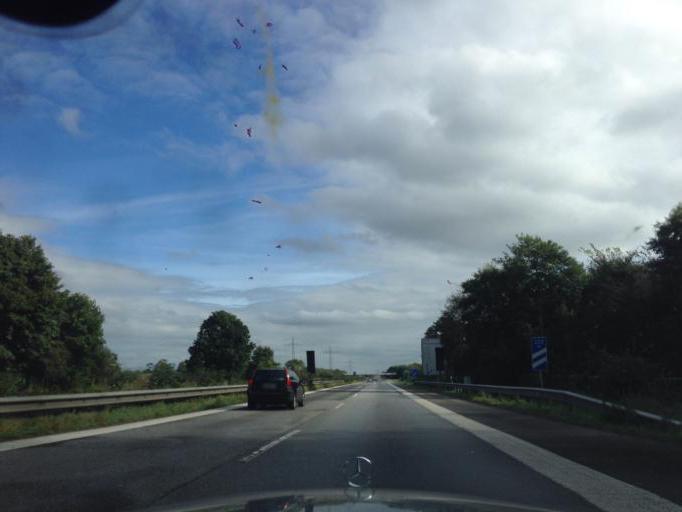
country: DE
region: Schleswig-Holstein
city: Borgstedt
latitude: 54.3510
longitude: 9.6927
